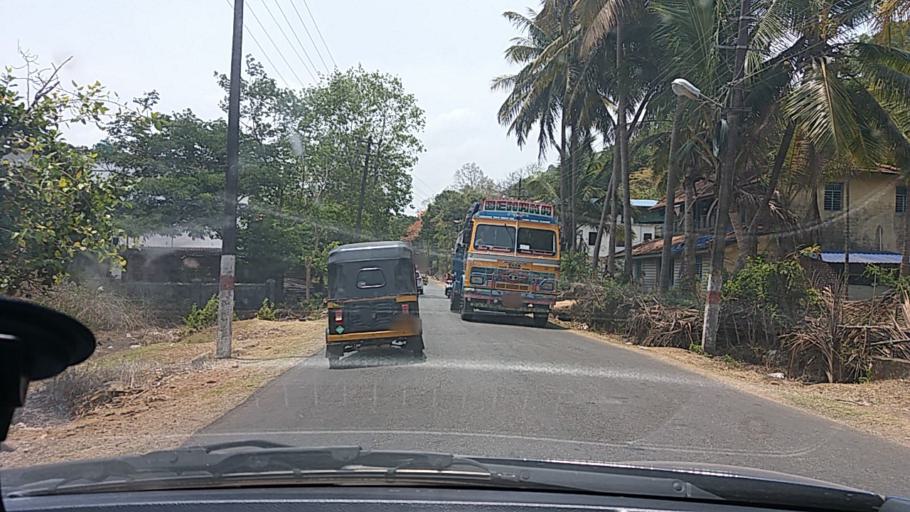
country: IN
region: Karnataka
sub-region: Uttar Kannada
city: Karwar
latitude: 14.8116
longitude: 74.1527
